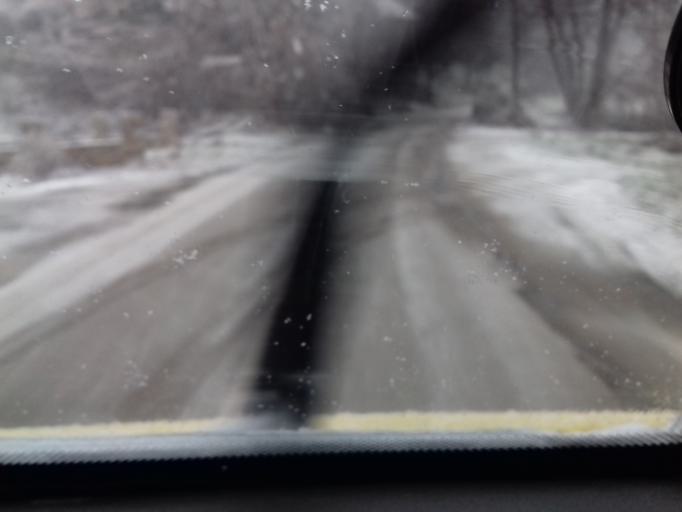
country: BA
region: Federation of Bosnia and Herzegovina
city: Lokvine
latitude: 44.2078
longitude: 17.8557
